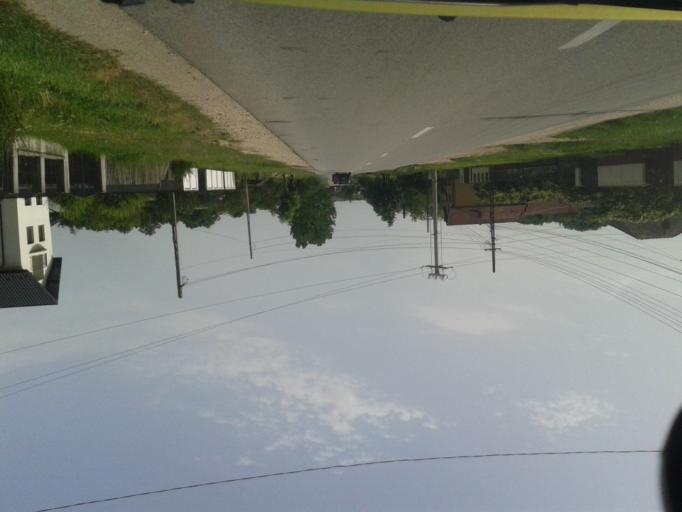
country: RO
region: Valcea
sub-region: Comuna Barbatesti
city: Bodesti
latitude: 45.1240
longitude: 24.1153
